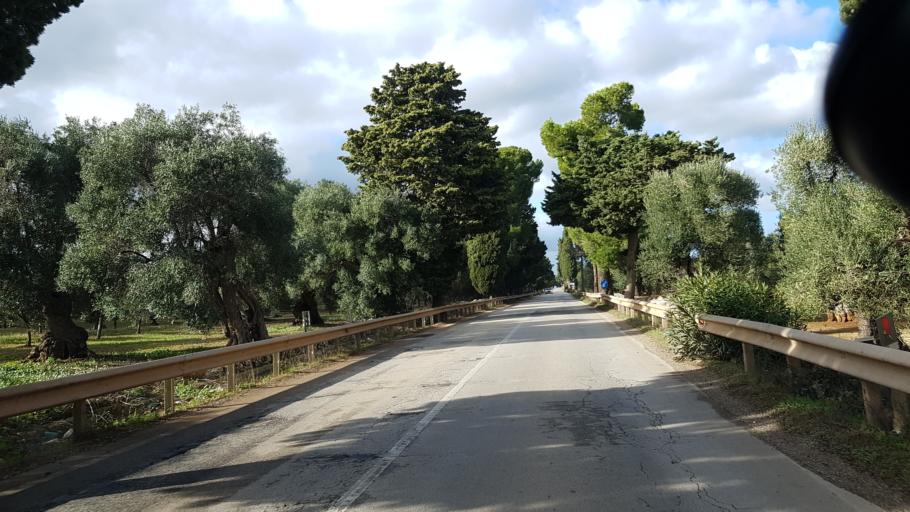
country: IT
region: Apulia
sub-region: Provincia di Brindisi
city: Ostuni
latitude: 40.7580
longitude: 17.5345
